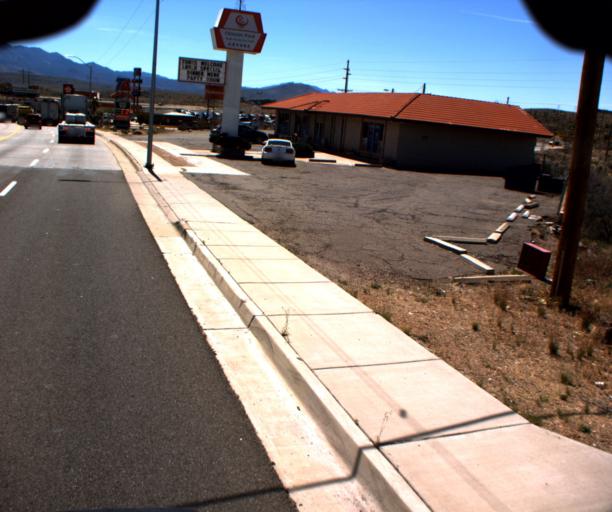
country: US
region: Arizona
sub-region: Mohave County
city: Kingman
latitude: 35.1927
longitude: -114.0713
